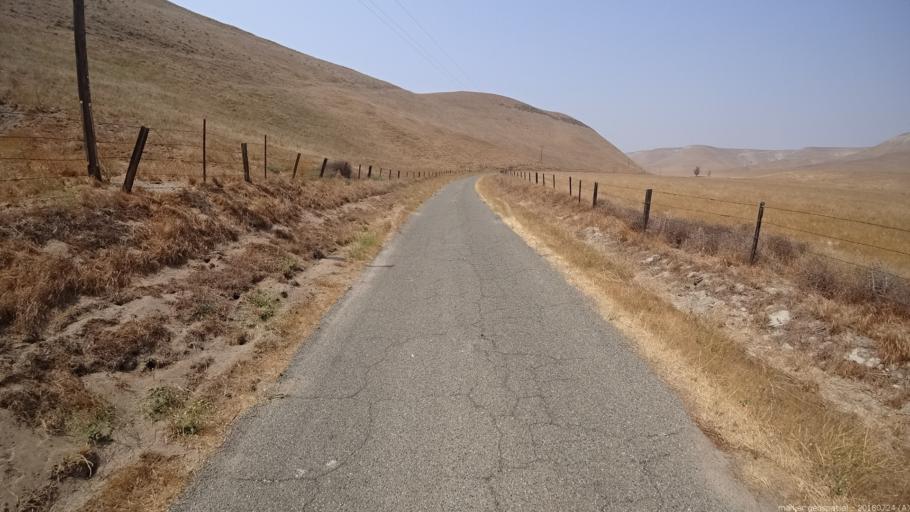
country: US
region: California
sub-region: Monterey County
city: King City
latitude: 36.1933
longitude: -120.9971
